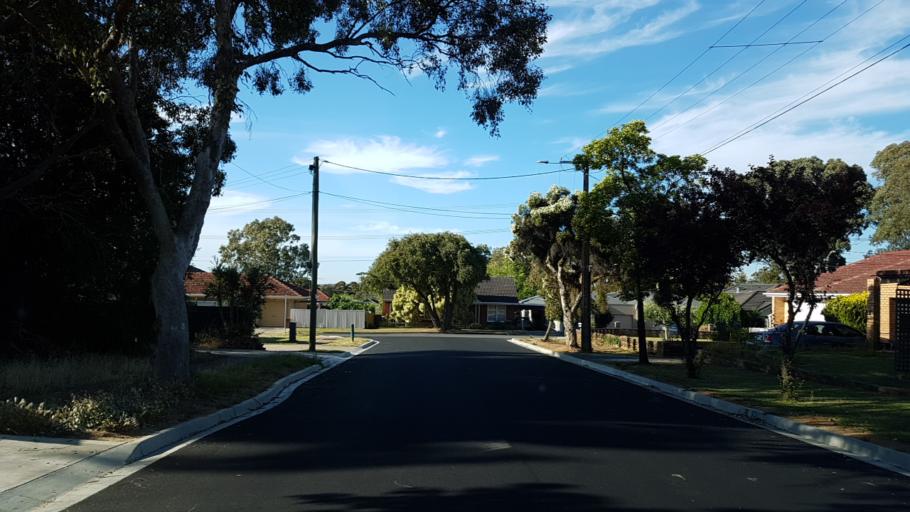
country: AU
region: South Australia
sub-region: Campbelltown
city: Campbelltown
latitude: -34.8976
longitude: 138.6809
